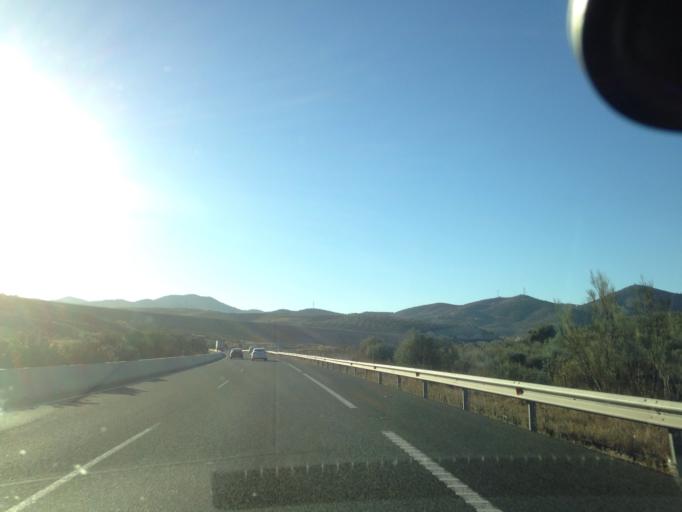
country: ES
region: Andalusia
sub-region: Provincia de Malaga
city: Casabermeja
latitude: 36.9183
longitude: -4.4459
